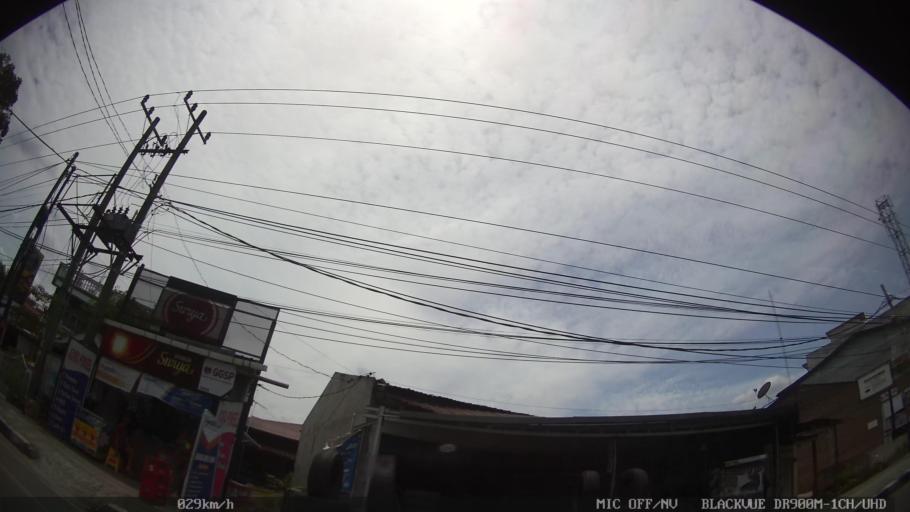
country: ID
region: North Sumatra
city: Sunggal
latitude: 3.5489
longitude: 98.6285
